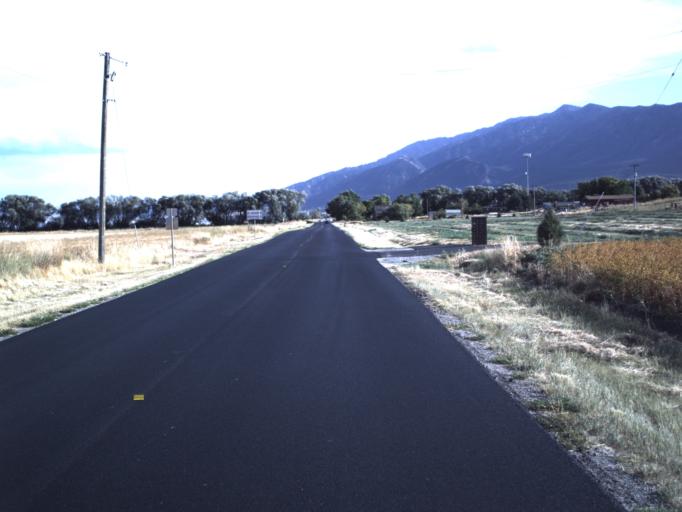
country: US
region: Utah
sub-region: Cache County
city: Mendon
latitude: 41.7487
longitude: -111.9794
